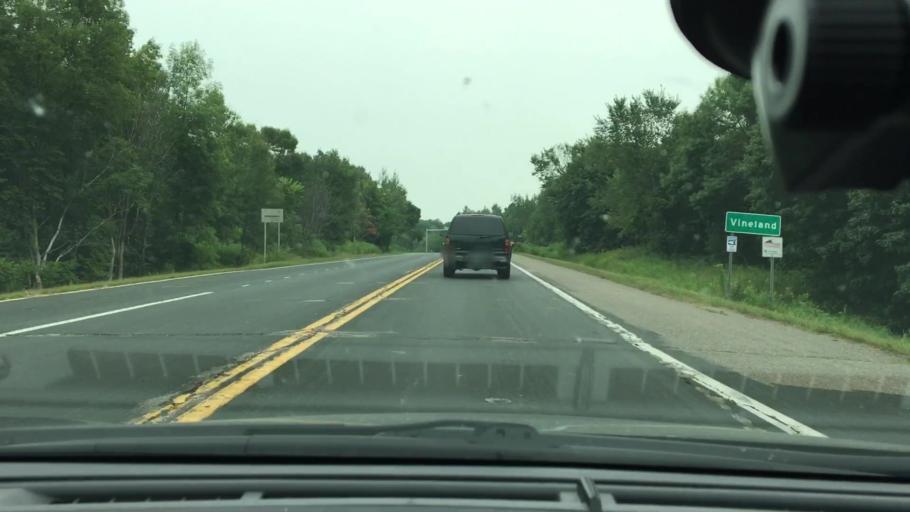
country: US
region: Minnesota
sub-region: Mille Lacs County
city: Vineland
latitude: 46.2059
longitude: -93.7854
